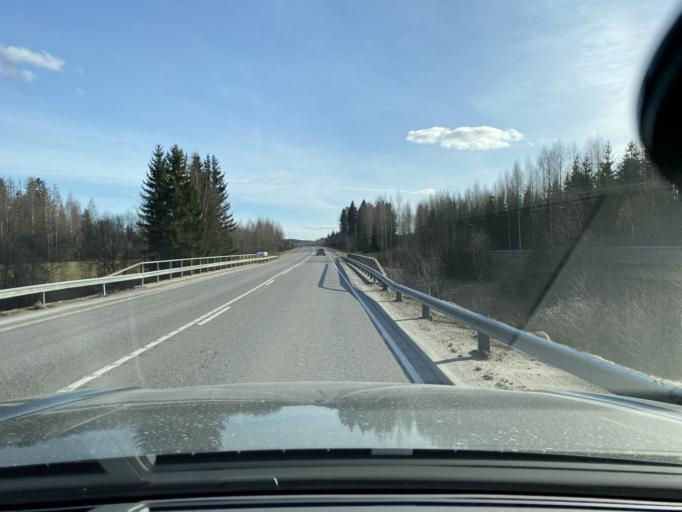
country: FI
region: Uusimaa
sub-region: Helsinki
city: Hyvinge
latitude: 60.6070
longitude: 24.8044
